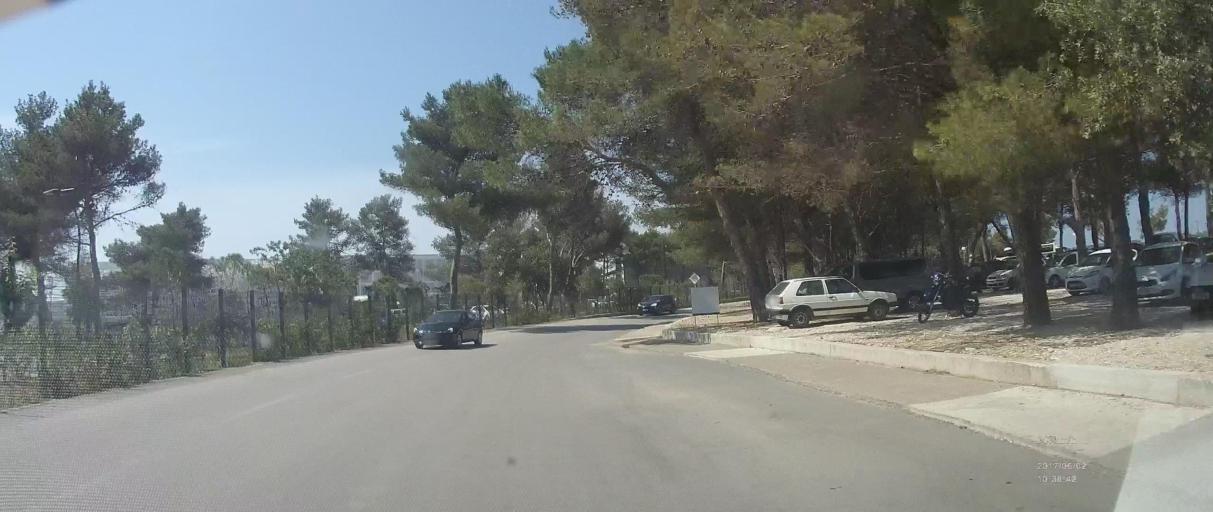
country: HR
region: Sibensko-Kniniska
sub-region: Grad Sibenik
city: Sibenik
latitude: 43.6980
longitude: 15.8882
